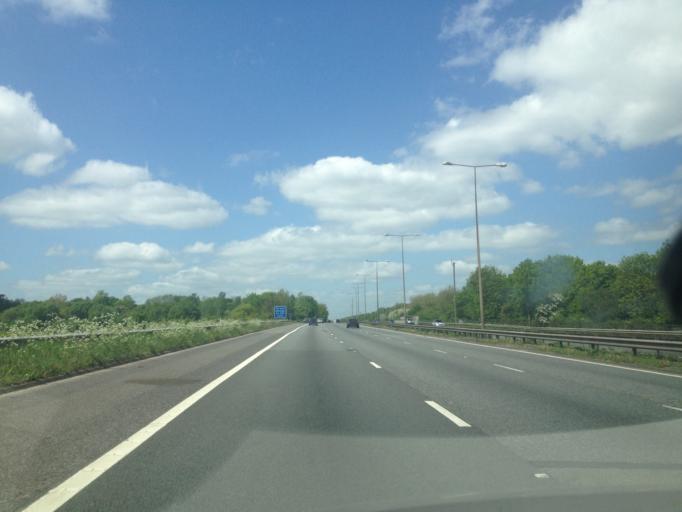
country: GB
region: England
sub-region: Hertfordshire
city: Elstree
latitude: 51.6411
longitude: -0.3197
